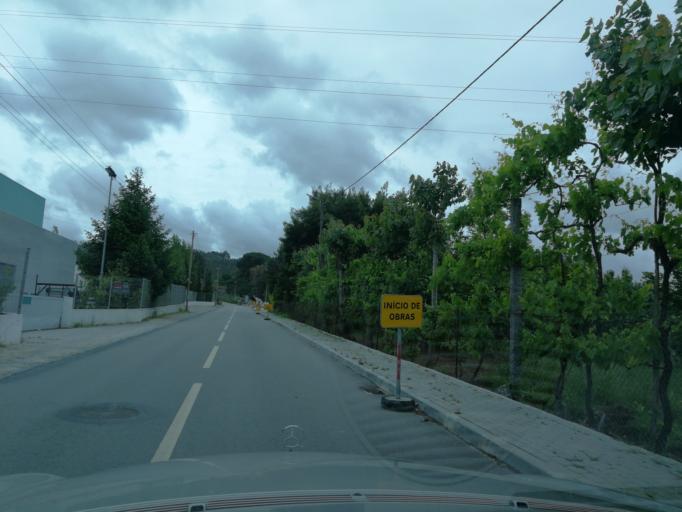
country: PT
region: Braga
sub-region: Braga
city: Adaufe
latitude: 41.6017
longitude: -8.3808
